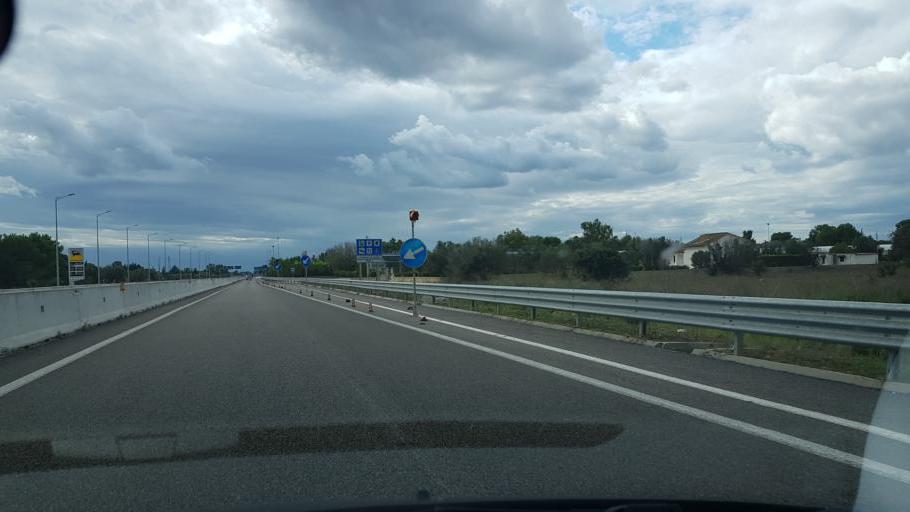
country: IT
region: Apulia
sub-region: Provincia di Lecce
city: Muro Leccese
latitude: 40.1249
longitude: 18.3363
